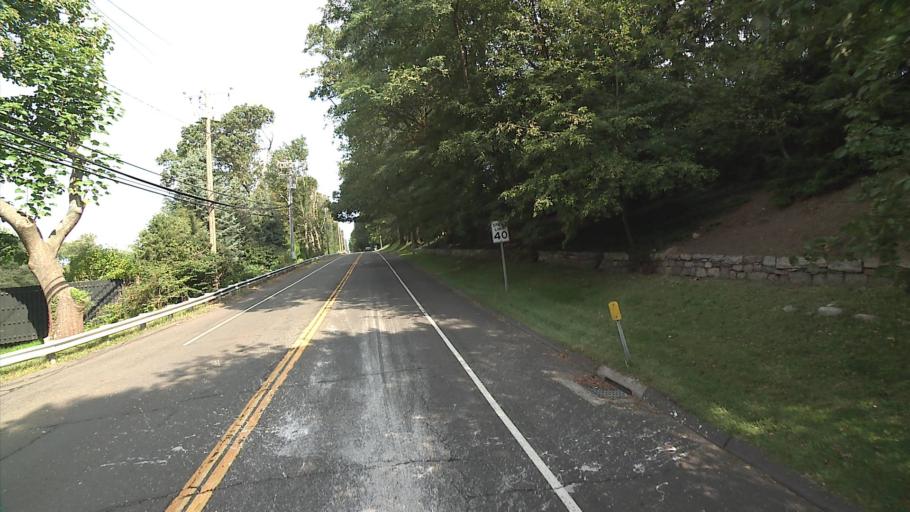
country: US
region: Connecticut
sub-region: Fairfield County
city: New Canaan
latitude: 41.1707
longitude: -73.4951
